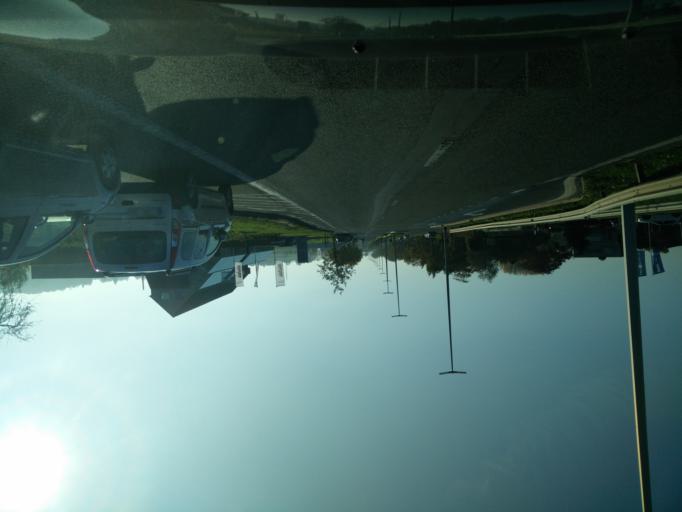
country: BE
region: Flanders
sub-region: Provincie Oost-Vlaanderen
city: Oudenaarde
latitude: 50.8242
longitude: 3.6037
